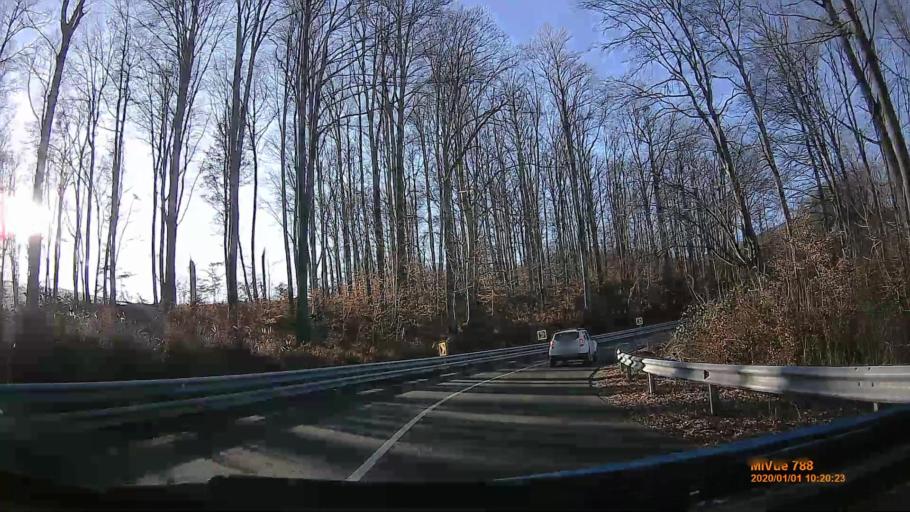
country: HU
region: Heves
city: Paradsasvar
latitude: 47.9001
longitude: 19.9876
